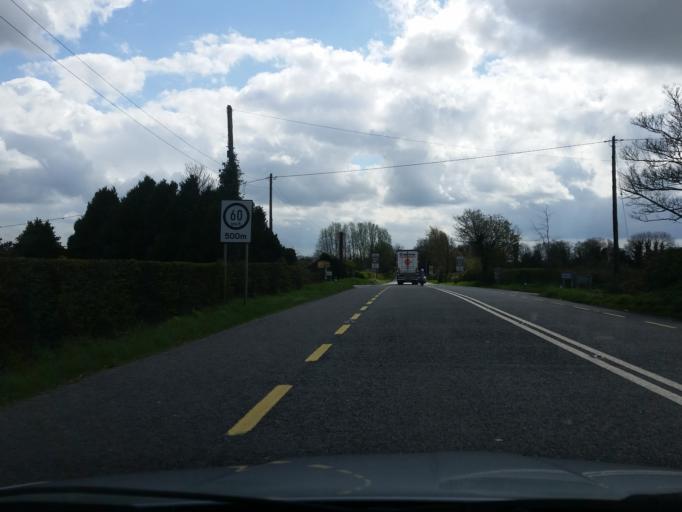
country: IE
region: Leinster
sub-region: An Mhi
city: Ratoath
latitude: 53.5650
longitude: -6.4447
